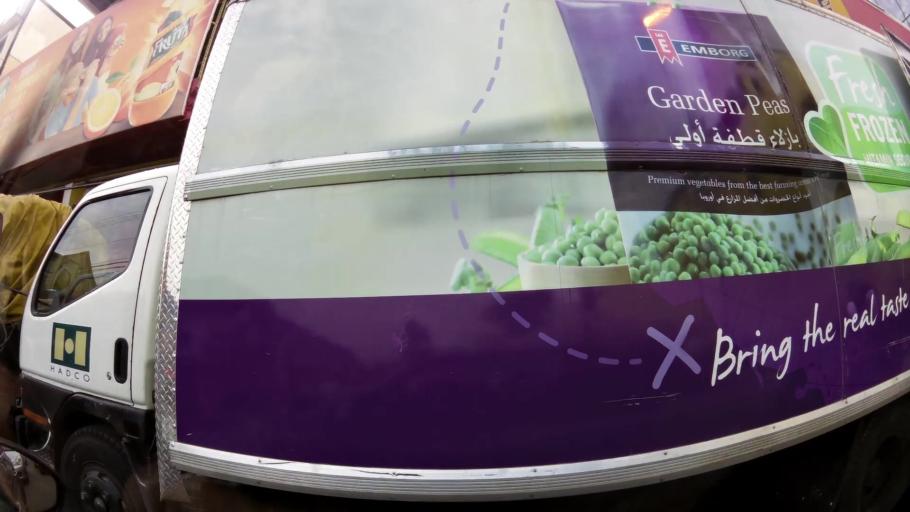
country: TT
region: San Juan/Laventille
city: Laventille
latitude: 10.6562
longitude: -61.5082
